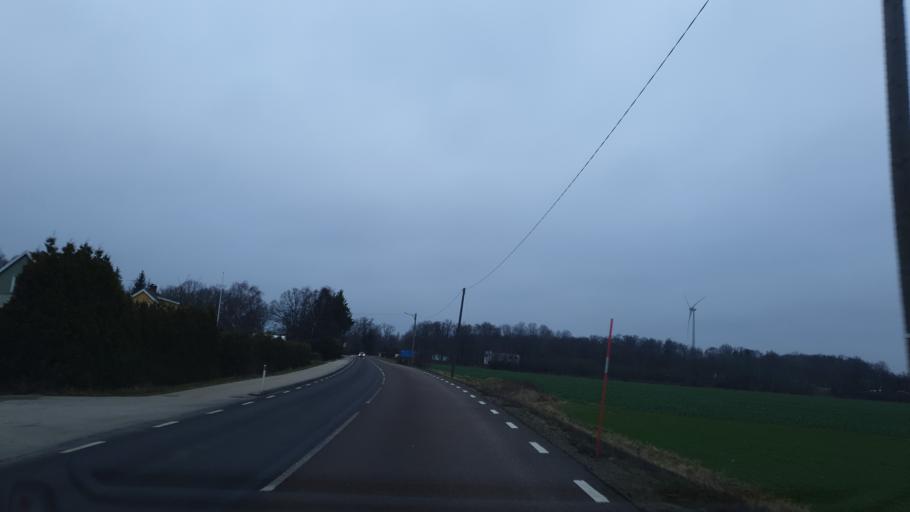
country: SE
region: Blekinge
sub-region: Karlskrona Kommun
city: Jaemjoe
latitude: 56.1806
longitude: 15.7210
